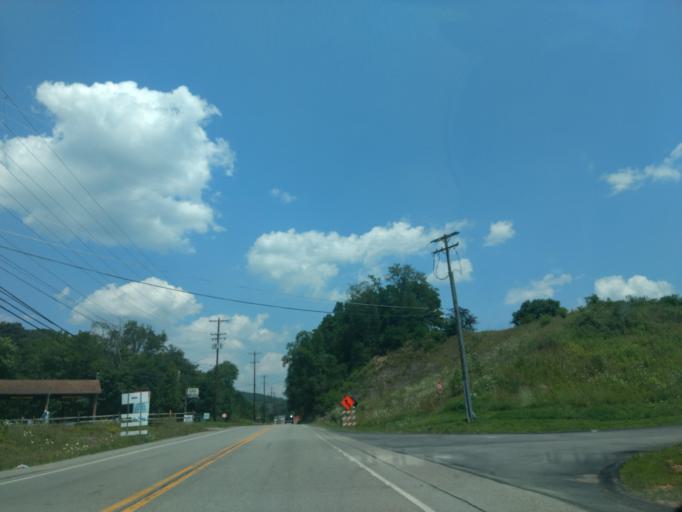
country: US
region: Pennsylvania
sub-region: Butler County
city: Zelienople
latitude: 40.8073
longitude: -80.1323
